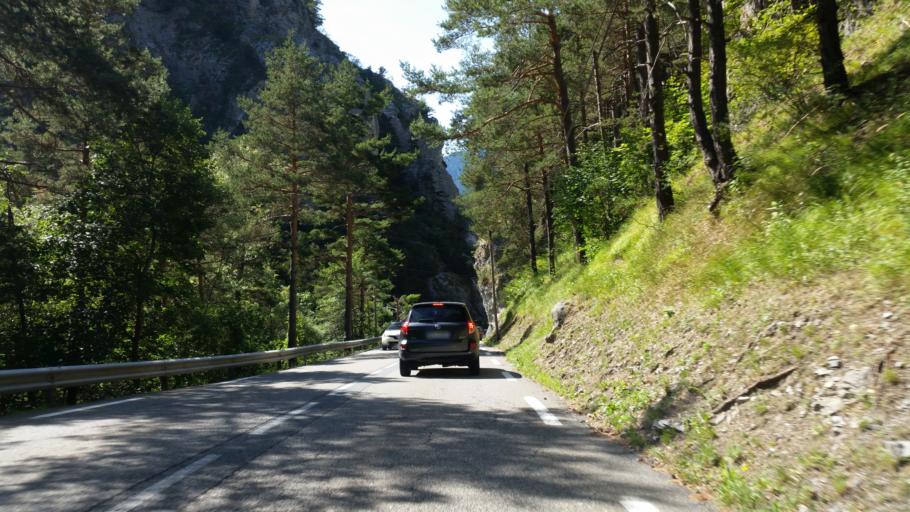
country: FR
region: Provence-Alpes-Cote d'Azur
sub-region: Departement des Alpes-Maritimes
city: Tende
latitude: 44.1260
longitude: 7.5675
